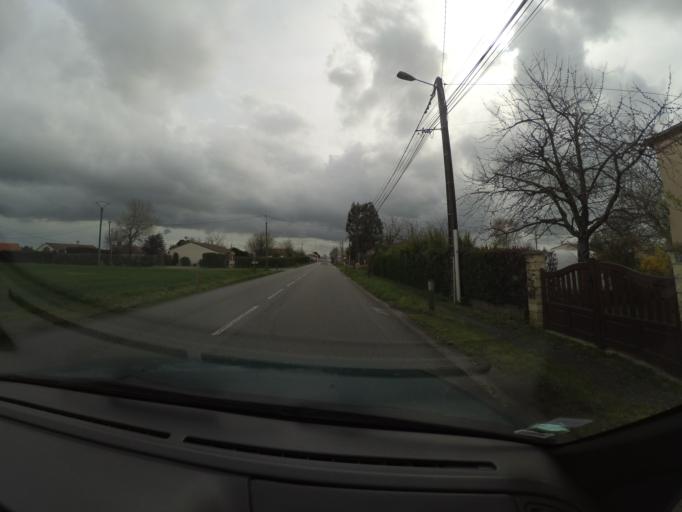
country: FR
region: Pays de la Loire
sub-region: Departement de la Loire-Atlantique
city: La Remaudiere
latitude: 47.2358
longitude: -1.2168
